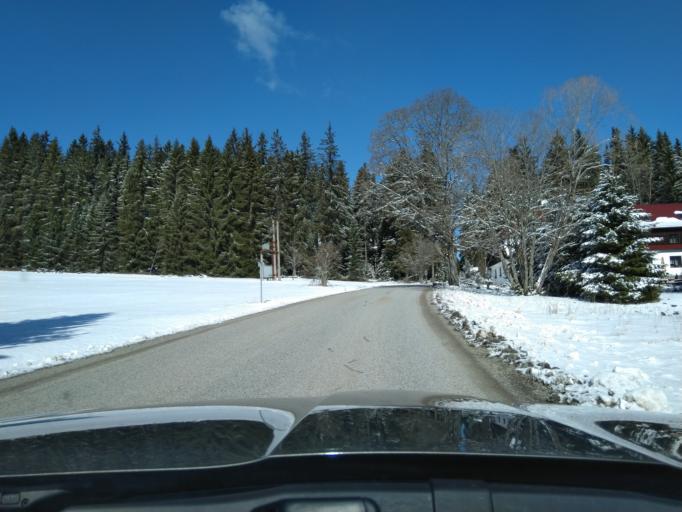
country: CZ
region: Jihocesky
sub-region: Okres Prachatice
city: Zdikov
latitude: 49.0482
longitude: 13.6637
